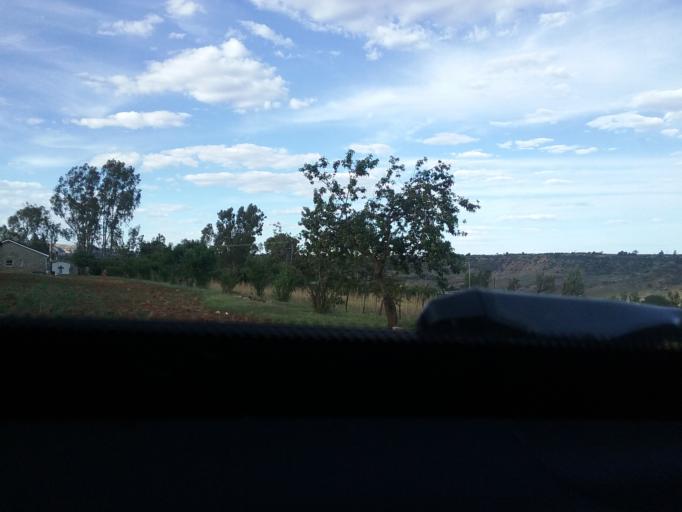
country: LS
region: Maseru
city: Maseru
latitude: -29.4258
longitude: 27.5730
